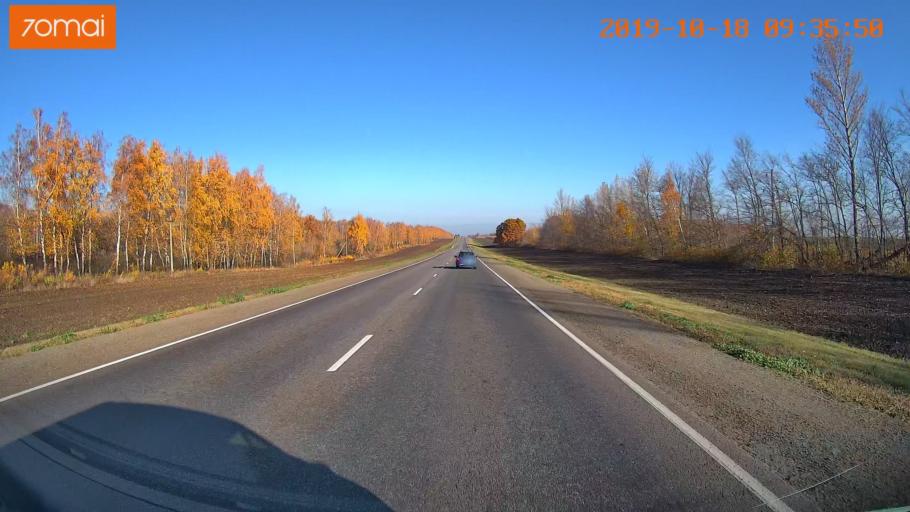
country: RU
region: Tula
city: Yefremov
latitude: 53.1975
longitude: 38.1473
